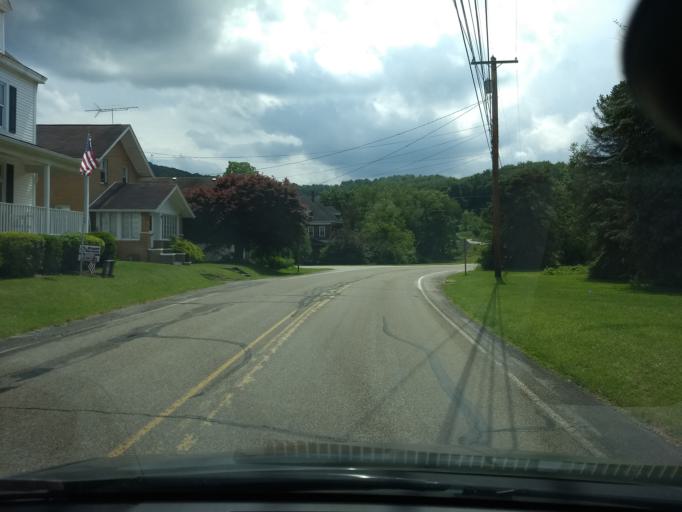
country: US
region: Pennsylvania
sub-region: Westmoreland County
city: Avonmore
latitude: 40.5211
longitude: -79.5002
